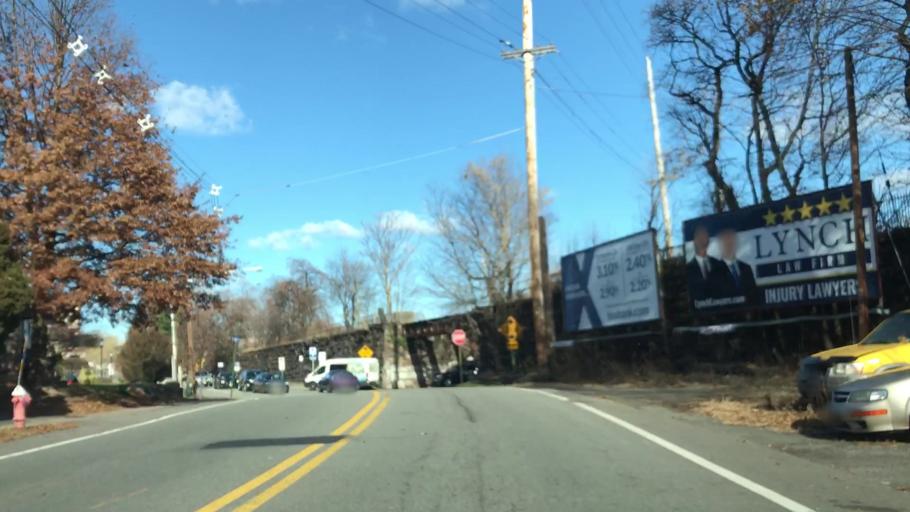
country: US
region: New Jersey
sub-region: Bergen County
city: Rutherford
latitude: 40.8254
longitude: -74.0997
